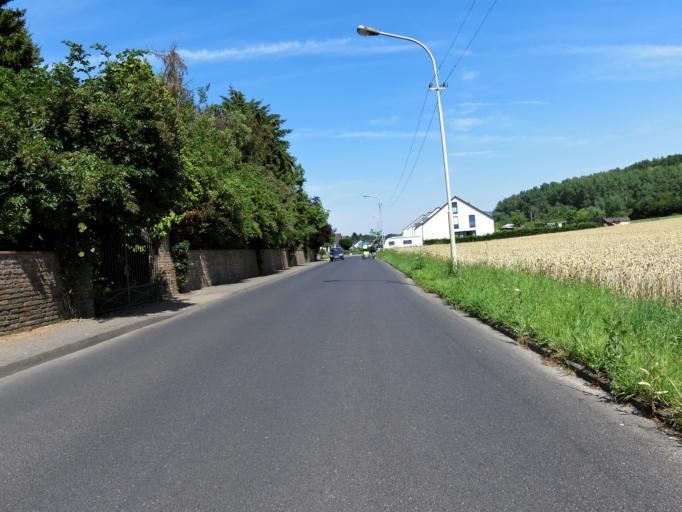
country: NL
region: Limburg
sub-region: Gemeente Kerkrade
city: Kerkrade
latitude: 50.8240
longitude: 6.0668
